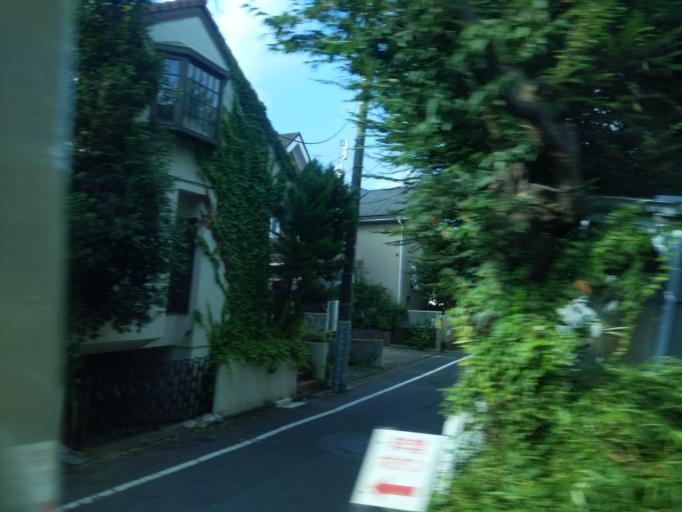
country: JP
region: Tokyo
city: Mitaka-shi
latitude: 35.6835
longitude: 139.6107
